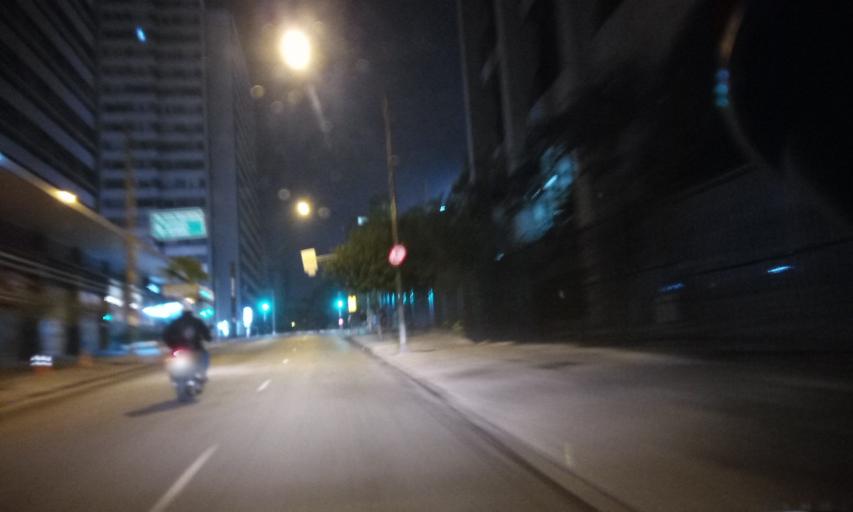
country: BR
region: Sao Paulo
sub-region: Sao Paulo
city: Sao Paulo
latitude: -23.5684
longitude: -46.6468
